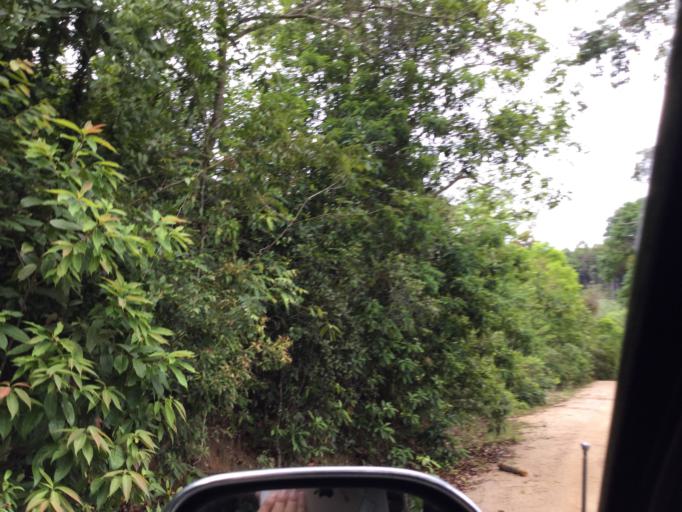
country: TH
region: Nakhon Si Thammarat
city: Ko Pha Ngan
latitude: 9.7377
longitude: 100.0584
